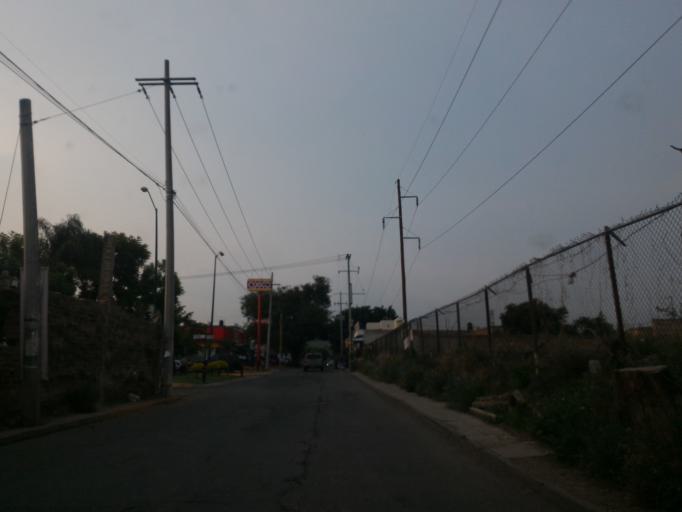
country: MX
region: Jalisco
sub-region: San Pedro Tlaquepaque
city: Paseo del Prado
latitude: 20.5902
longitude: -103.3898
